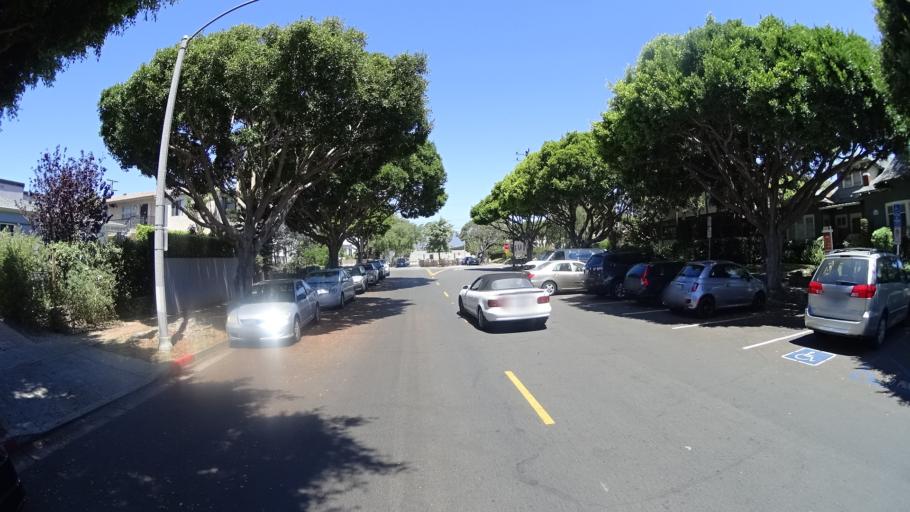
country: US
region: California
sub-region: Los Angeles County
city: Santa Monica
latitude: 34.0150
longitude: -118.4825
